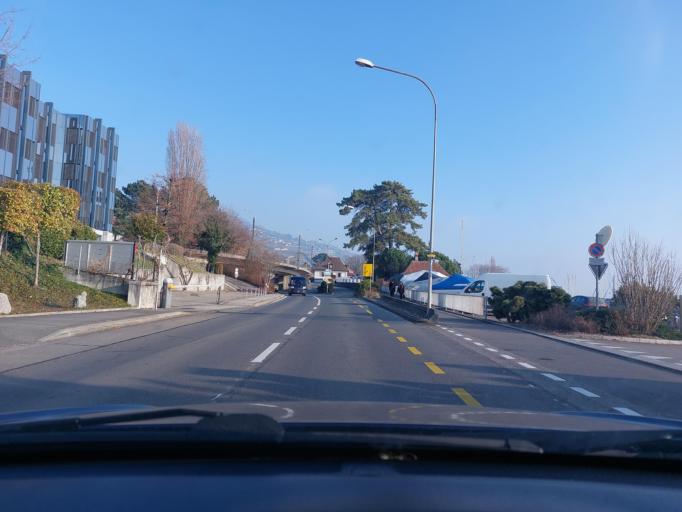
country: CH
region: Vaud
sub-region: Lavaux-Oron District
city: Lutry
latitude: 46.5042
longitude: 6.6774
